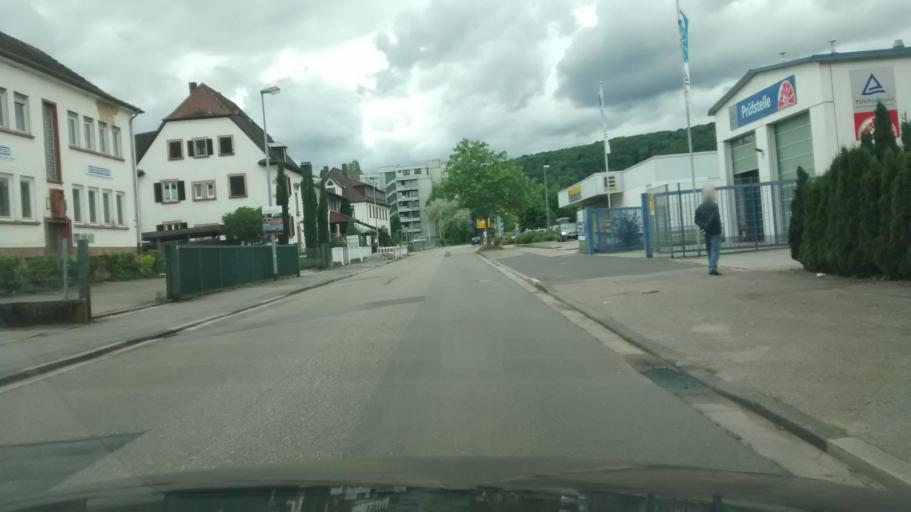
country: DE
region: Rheinland-Pfalz
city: Bad Bergzabern
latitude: 49.1019
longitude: 8.0064
